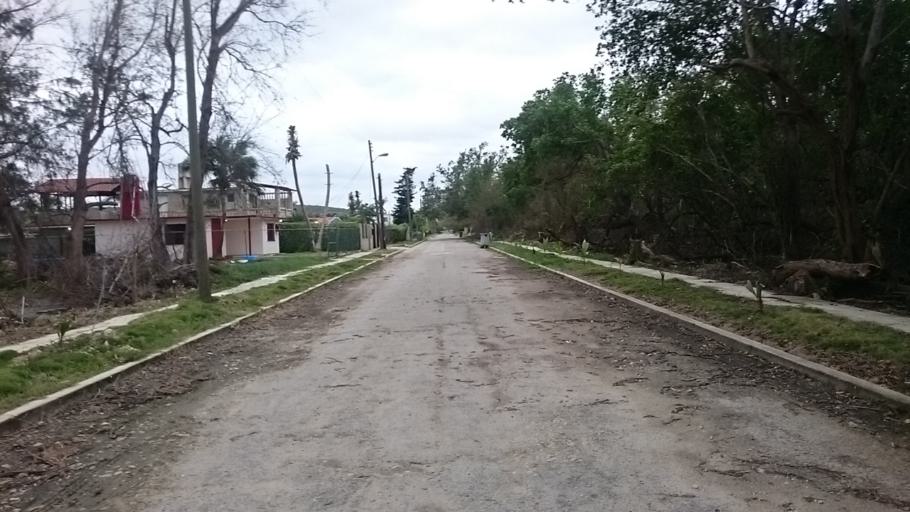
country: CU
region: Mayabeque
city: Jaruco
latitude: 23.1740
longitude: -82.1080
